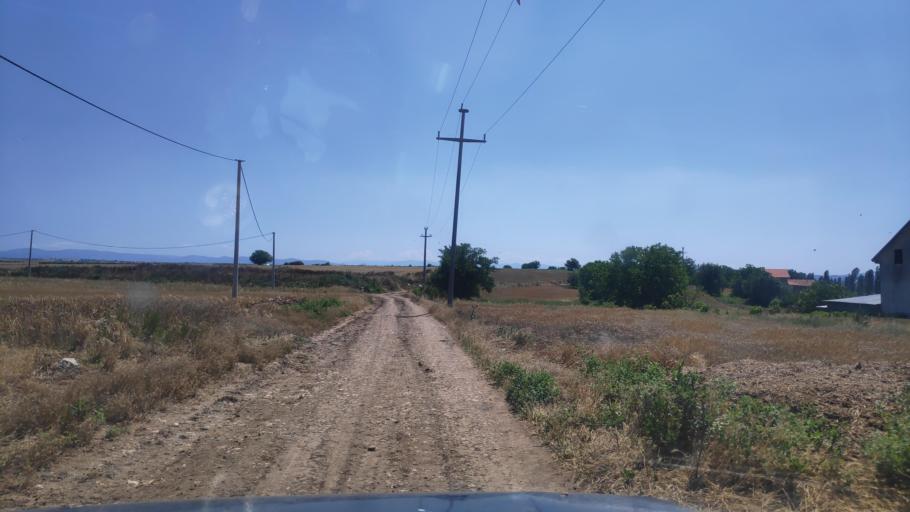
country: MK
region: Kumanovo
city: Bedinje
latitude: 42.1574
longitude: 21.6800
